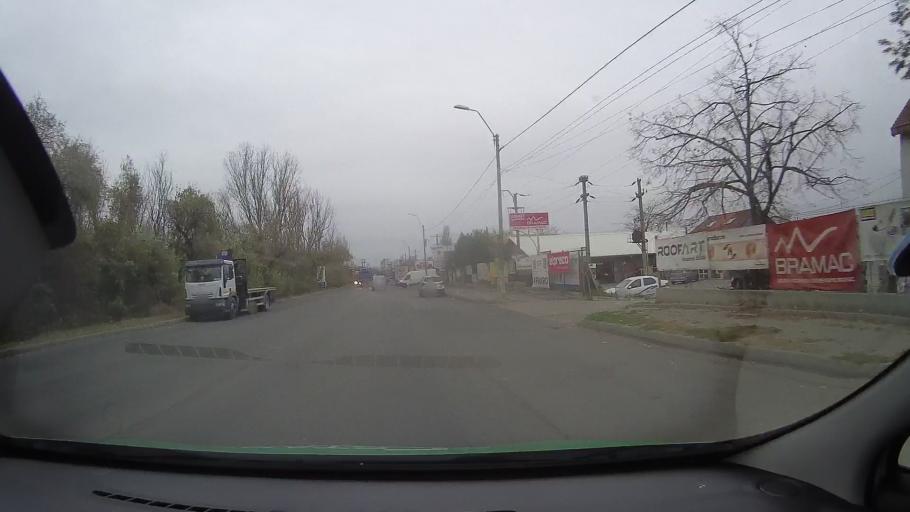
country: RO
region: Ialomita
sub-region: Comuna Slobozia
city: Slobozia
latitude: 44.5753
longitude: 27.3863
